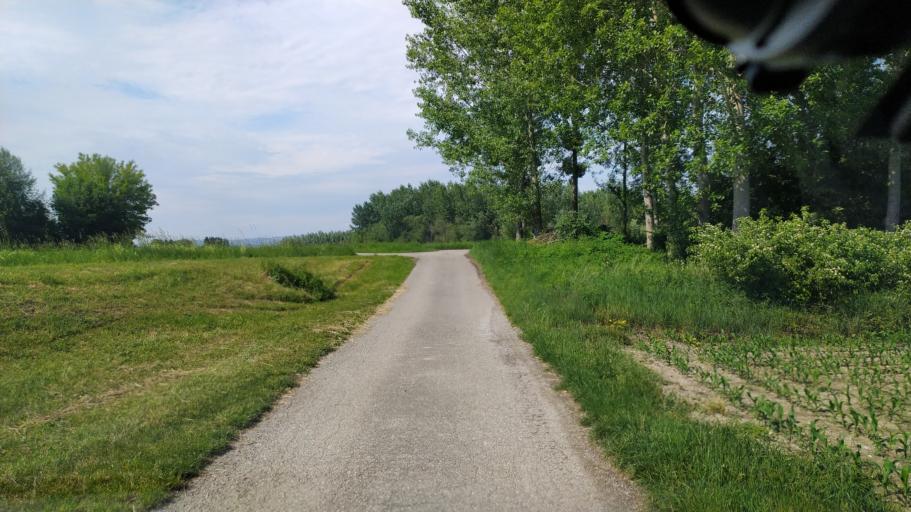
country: AT
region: Lower Austria
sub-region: Politischer Bezirk Amstetten
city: Strengberg
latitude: 48.1753
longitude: 14.6935
